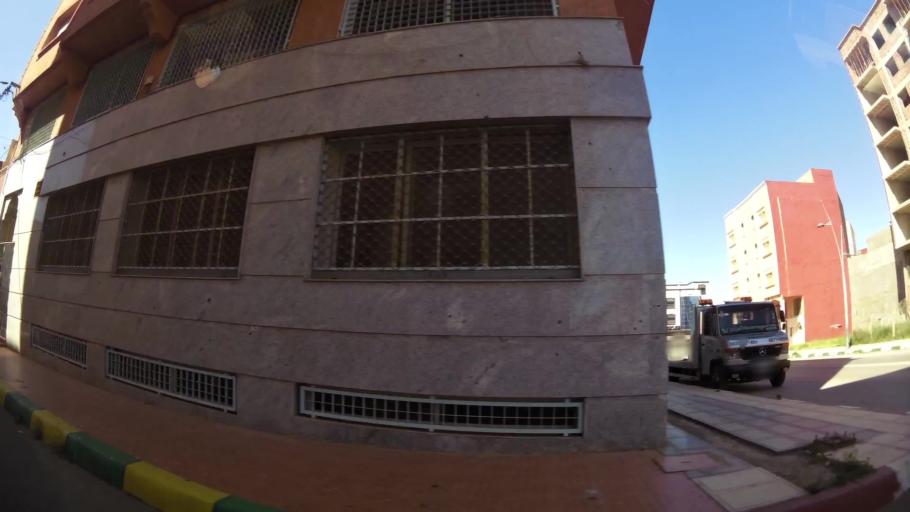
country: MA
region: Oriental
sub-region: Berkane-Taourirt
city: Berkane
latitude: 34.9368
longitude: -2.3228
